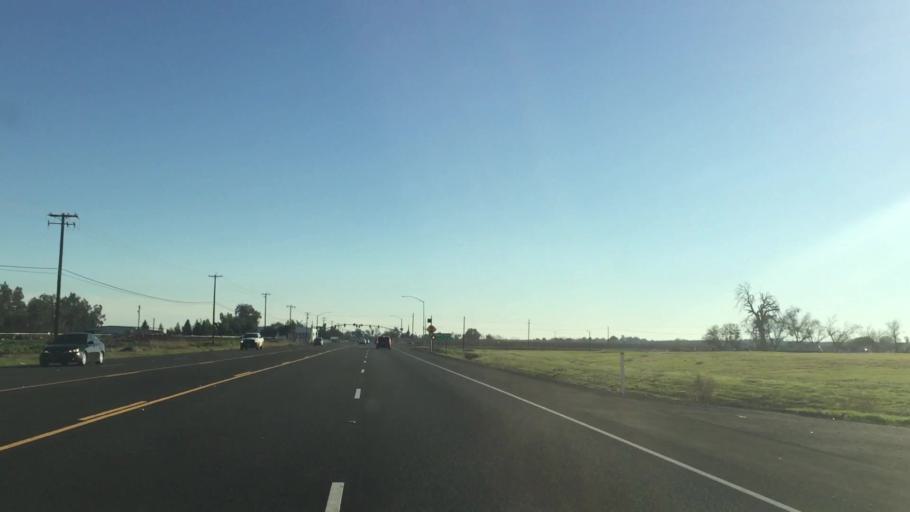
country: US
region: California
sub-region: Butte County
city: Gridley
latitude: 39.3679
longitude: -121.6092
